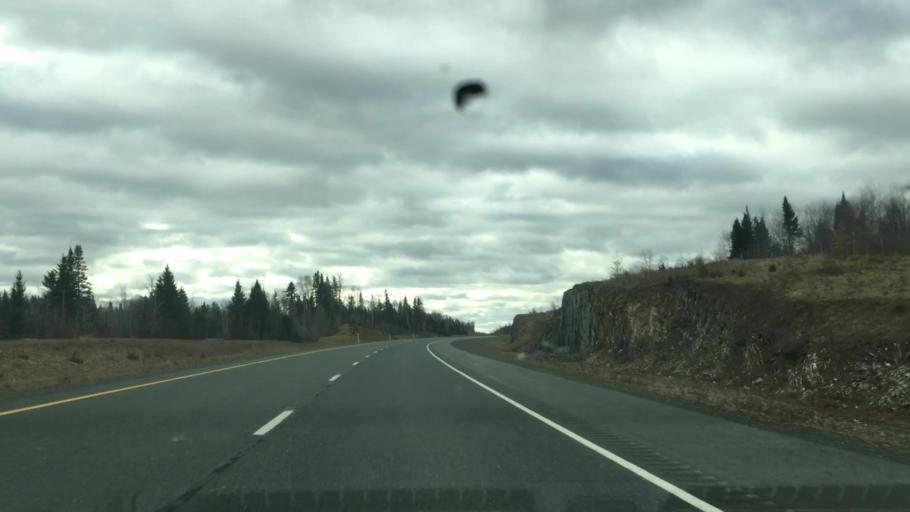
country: US
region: Maine
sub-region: Aroostook County
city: Easton
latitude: 46.6182
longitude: -67.7399
